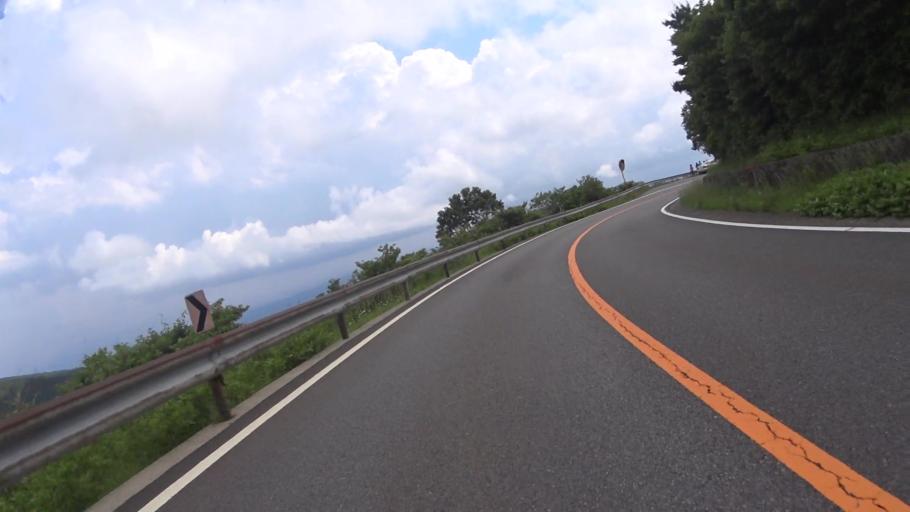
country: JP
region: Kumamoto
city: Aso
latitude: 33.0863
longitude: 131.1933
